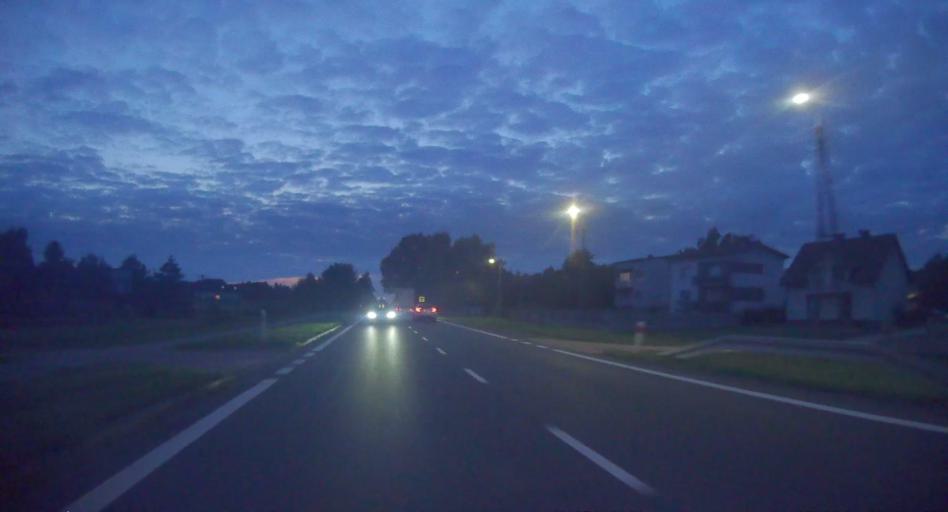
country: PL
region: Silesian Voivodeship
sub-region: Powiat klobucki
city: Kamyk
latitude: 50.8696
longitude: 19.0108
